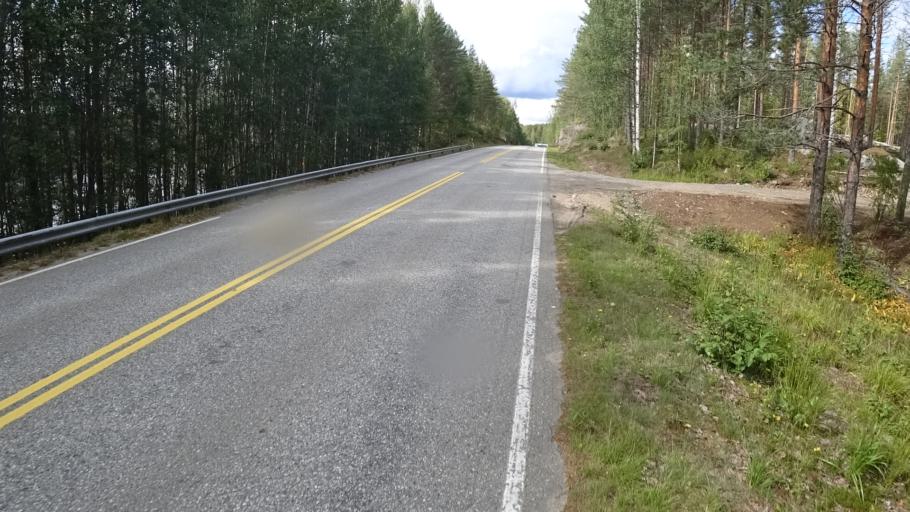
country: FI
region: North Karelia
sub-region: Joensuu
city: Ilomantsi
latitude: 62.6191
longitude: 31.2024
